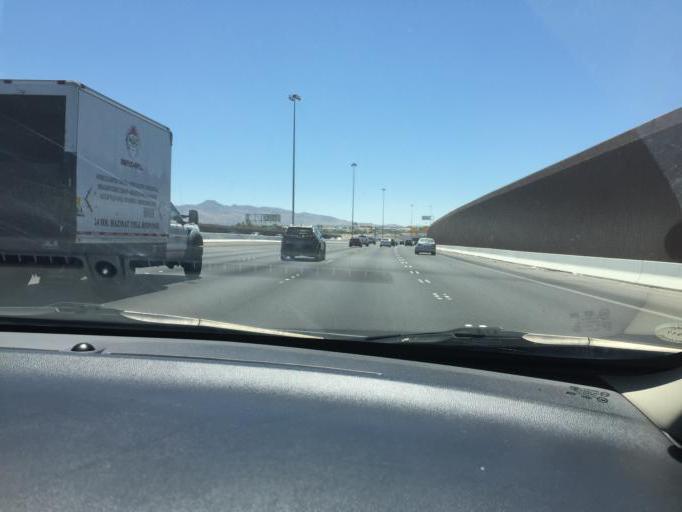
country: US
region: Nevada
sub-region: Clark County
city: Paradise
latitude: 36.0488
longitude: -115.1354
